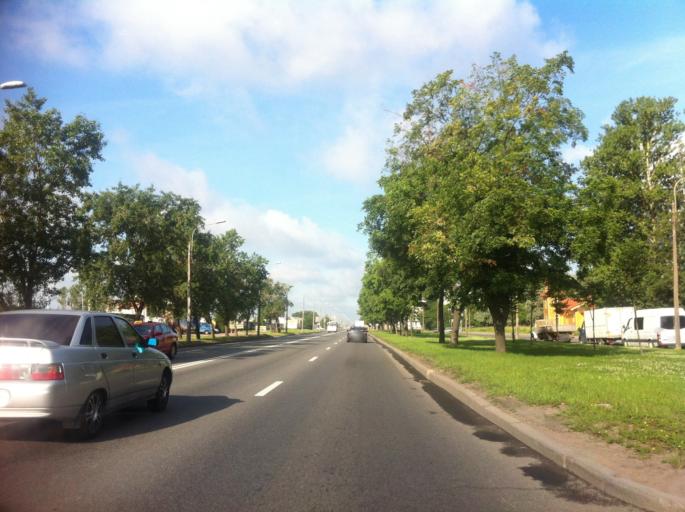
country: RU
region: St.-Petersburg
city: Dachnoye
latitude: 59.8331
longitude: 30.2575
